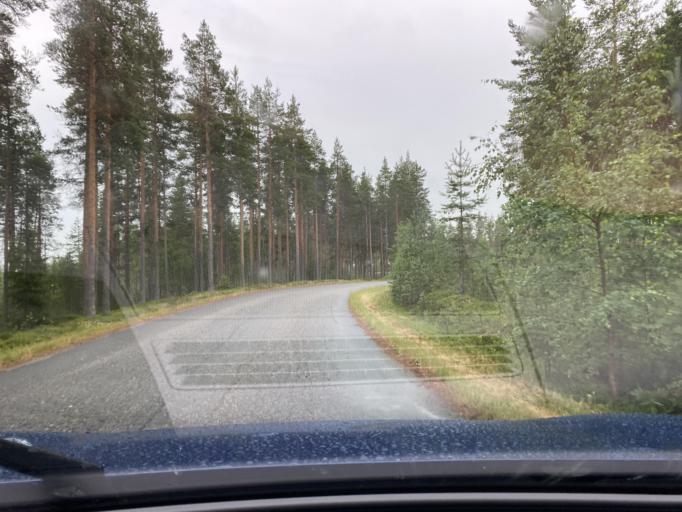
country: FI
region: Central Ostrobothnia
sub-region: Kaustinen
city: Halsua
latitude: 63.4111
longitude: 23.9740
